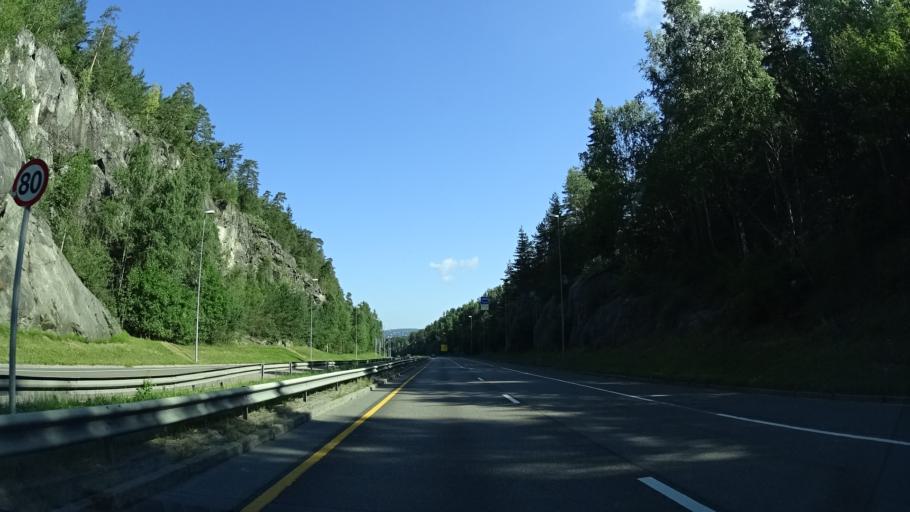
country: NO
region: Akershus
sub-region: Oppegard
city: Kolbotn
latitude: 59.8284
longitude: 10.7778
